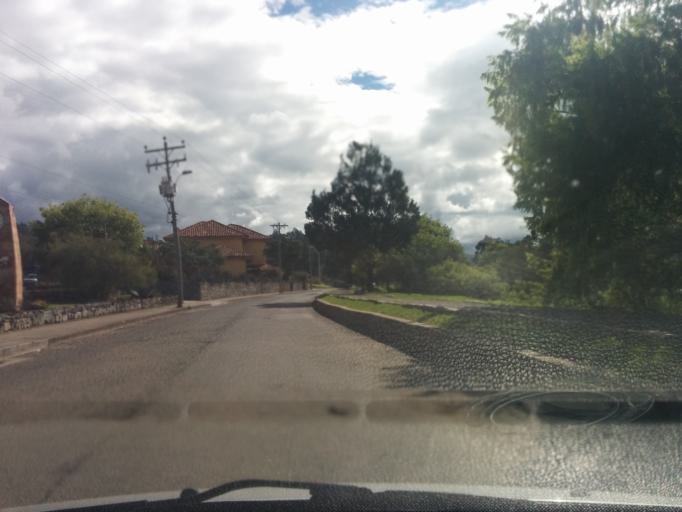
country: EC
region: Azuay
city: Cuenca
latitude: -2.9147
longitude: -78.9926
